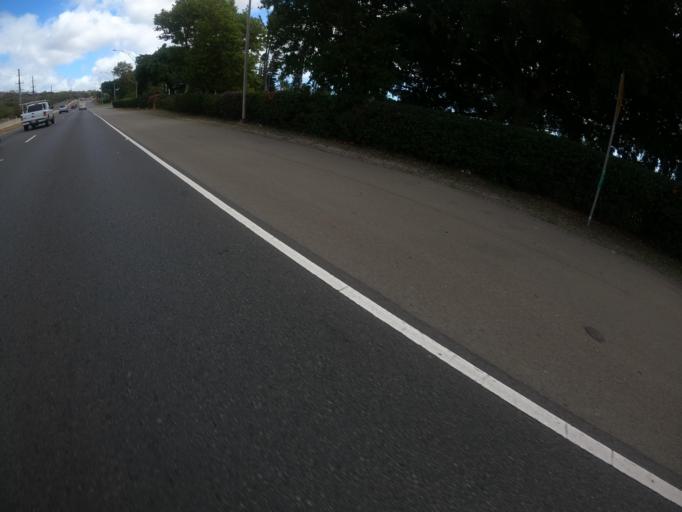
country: US
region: Hawaii
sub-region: Honolulu County
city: Makakilo City
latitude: 21.3441
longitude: -158.1168
